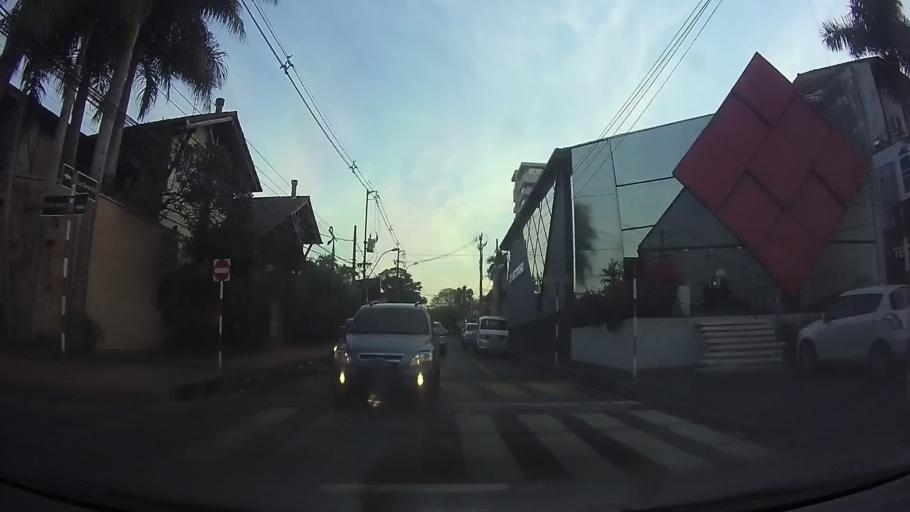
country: PY
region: Central
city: Fernando de la Mora
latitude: -25.3000
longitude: -57.5648
